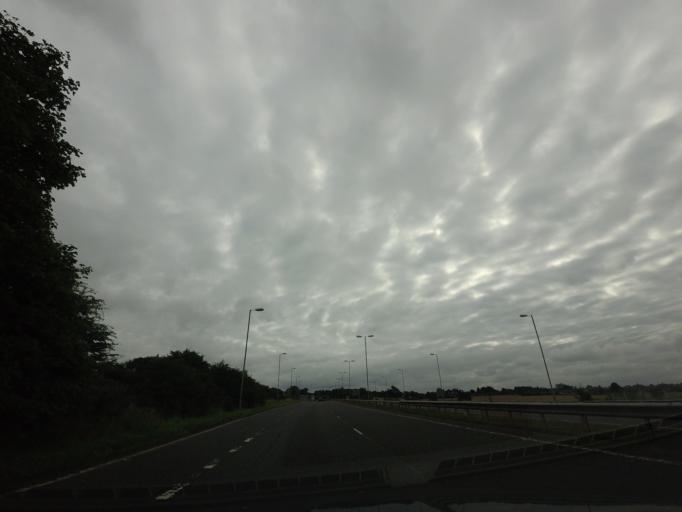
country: GB
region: Scotland
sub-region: Dumfries and Galloway
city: Gretna
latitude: 55.0002
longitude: -3.0701
